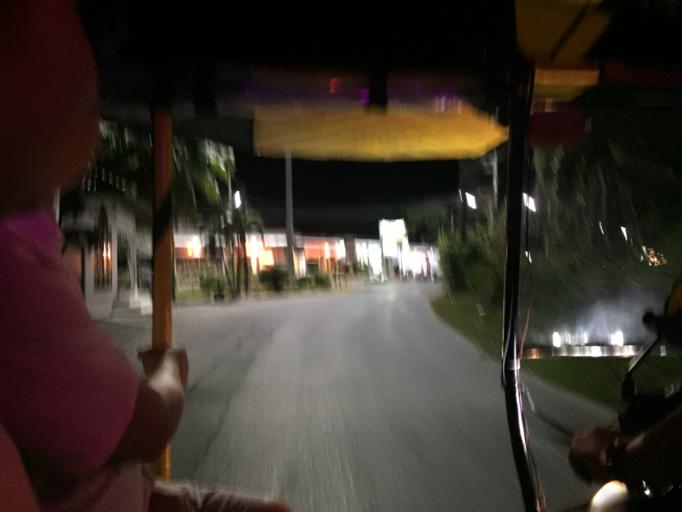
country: TH
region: Phuket
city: Thalang
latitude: 7.9856
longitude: 98.2926
